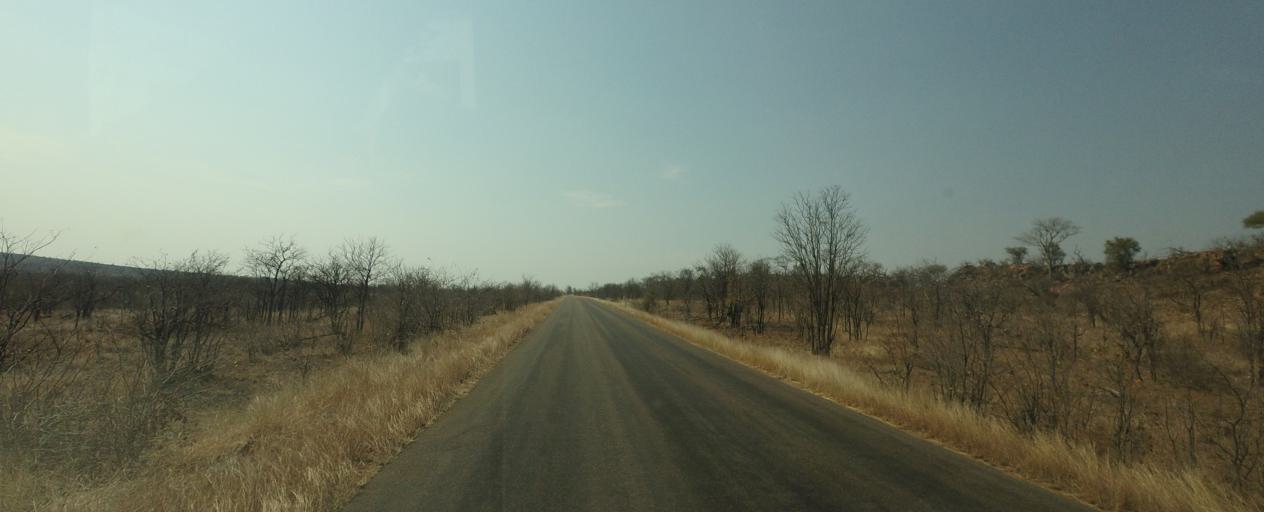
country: ZA
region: Limpopo
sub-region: Mopani District Municipality
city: Phalaborwa
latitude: -23.9590
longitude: 31.6245
